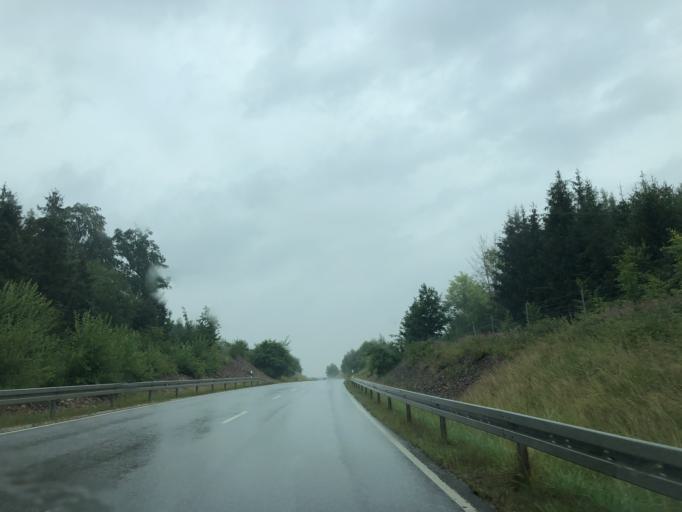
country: DE
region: Bavaria
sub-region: Upper Bavaria
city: Au in der Hallertau
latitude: 48.5459
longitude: 11.7400
